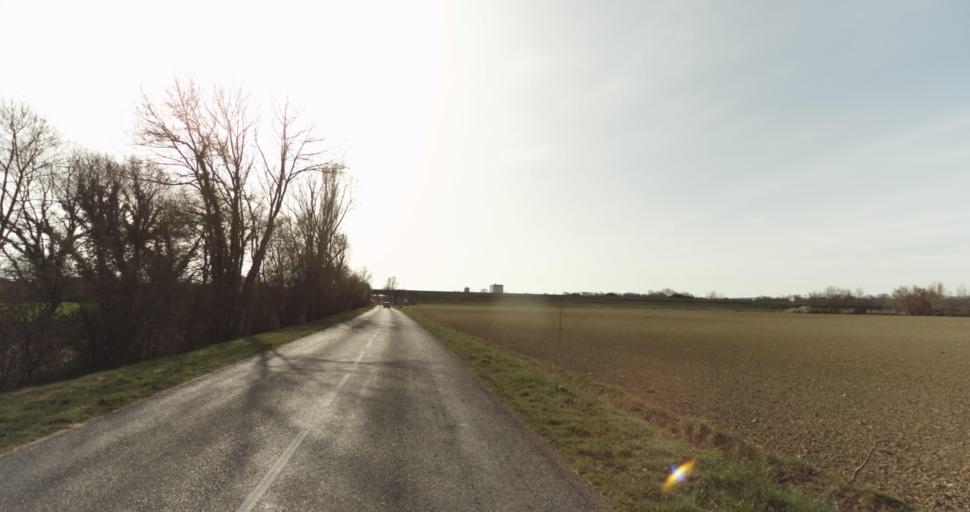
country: FR
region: Midi-Pyrenees
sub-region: Departement du Tarn
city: Saint-Sulpice-la-Pointe
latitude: 43.7668
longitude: 1.7183
